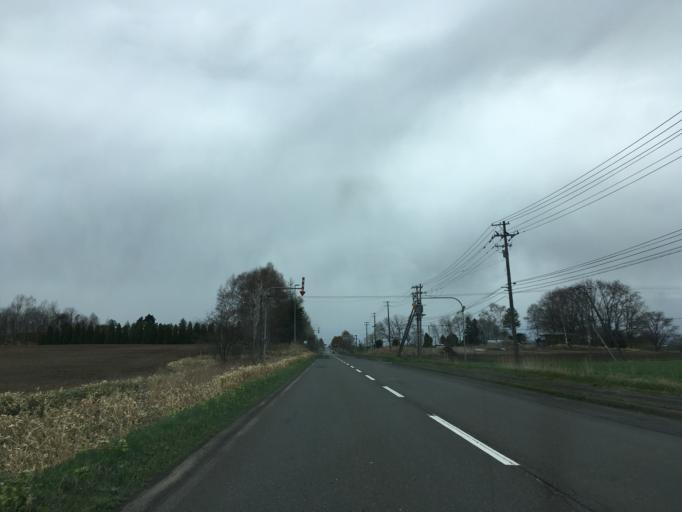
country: JP
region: Hokkaido
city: Chitose
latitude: 42.9111
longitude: 141.8112
